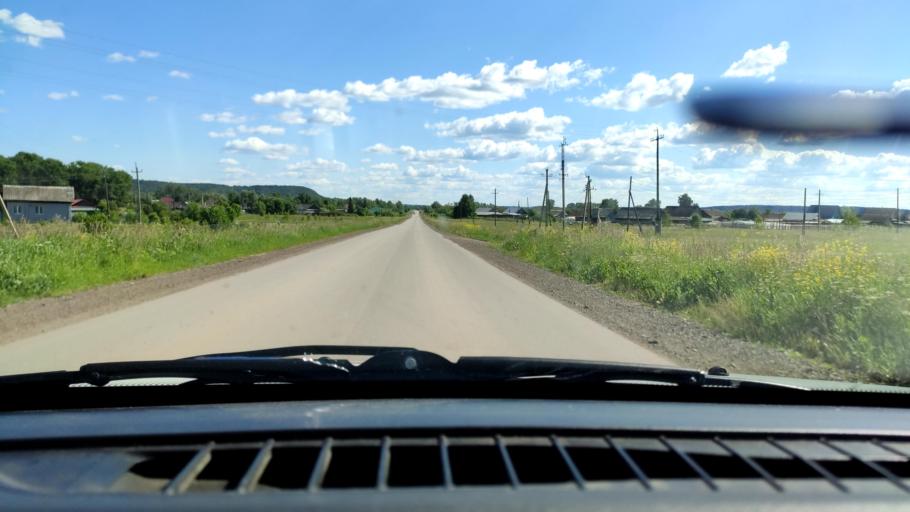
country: RU
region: Perm
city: Orda
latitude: 57.2187
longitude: 56.5753
